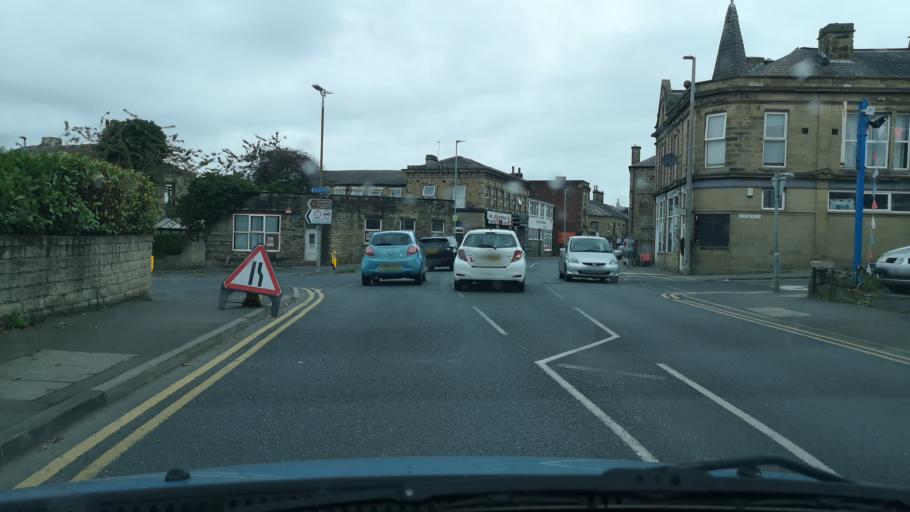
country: GB
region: England
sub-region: Kirklees
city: Heckmondwike
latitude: 53.7050
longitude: -1.6734
